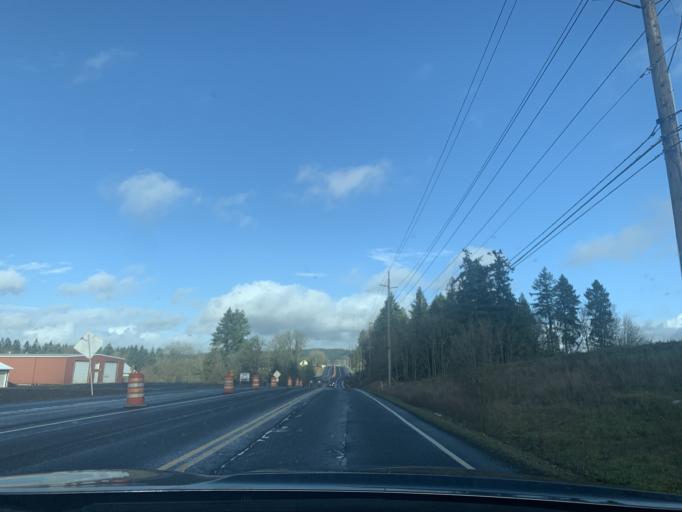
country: US
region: Oregon
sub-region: Washington County
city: King City
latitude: 45.4044
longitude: -122.8516
